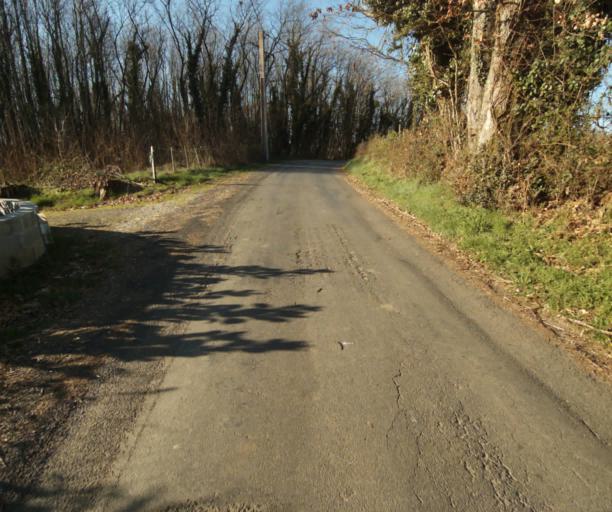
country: FR
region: Limousin
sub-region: Departement de la Correze
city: Uzerche
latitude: 45.3905
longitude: 1.5922
